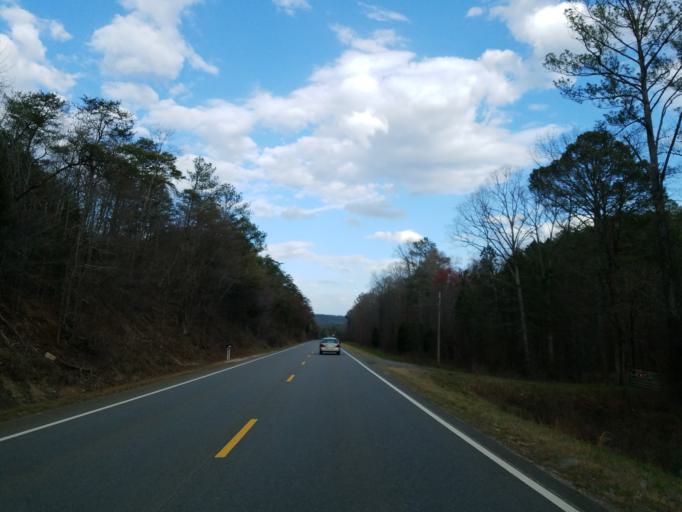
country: US
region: Georgia
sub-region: Bartow County
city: Rydal
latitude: 34.4482
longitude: -84.7338
